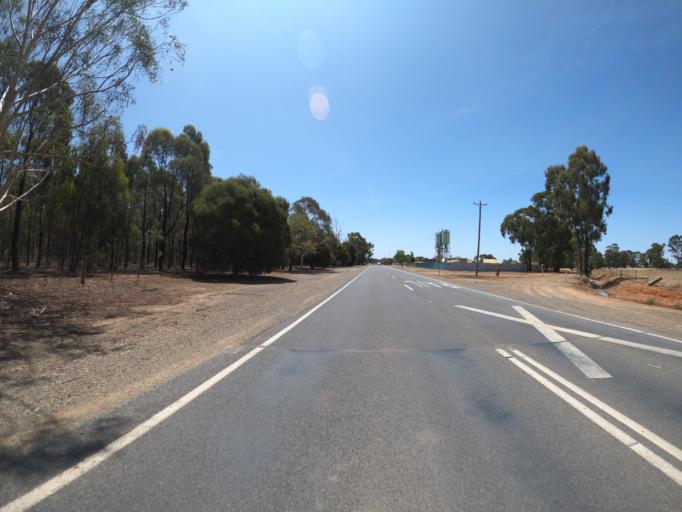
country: AU
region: Victoria
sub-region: Moira
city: Yarrawonga
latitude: -36.0254
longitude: 145.9955
